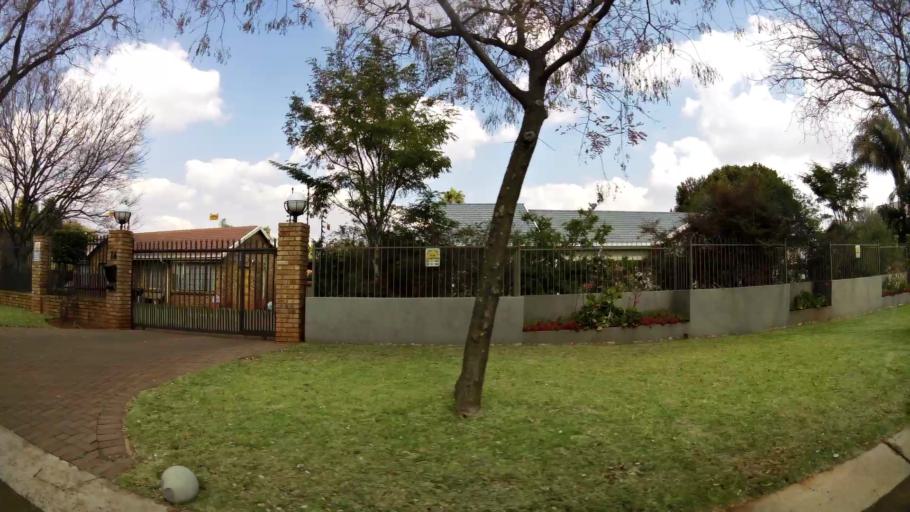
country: ZA
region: Gauteng
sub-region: City of Tshwane Metropolitan Municipality
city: Centurion
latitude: -25.8341
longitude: 28.2367
